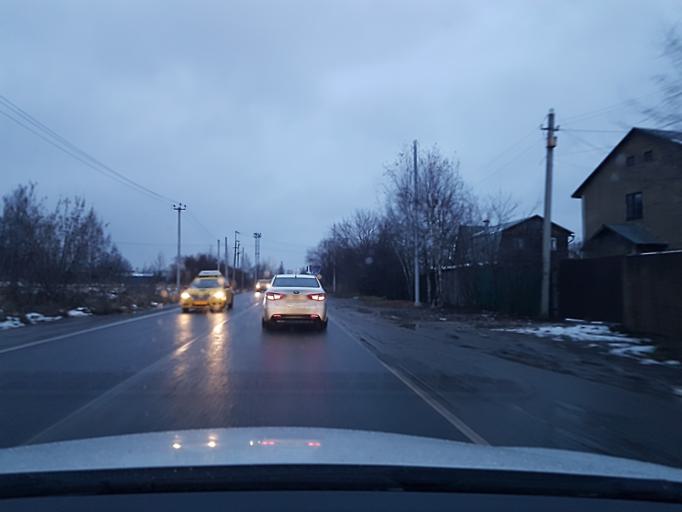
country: RU
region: Moskovskaya
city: Sheremet'yevskiy
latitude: 55.9692
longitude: 37.4795
